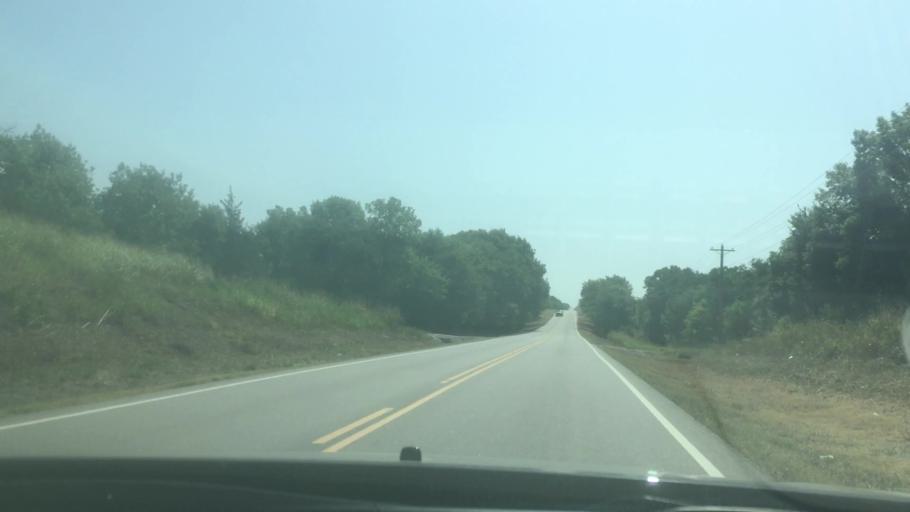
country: US
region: Oklahoma
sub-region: Bryan County
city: Durant
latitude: 34.1427
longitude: -96.3920
